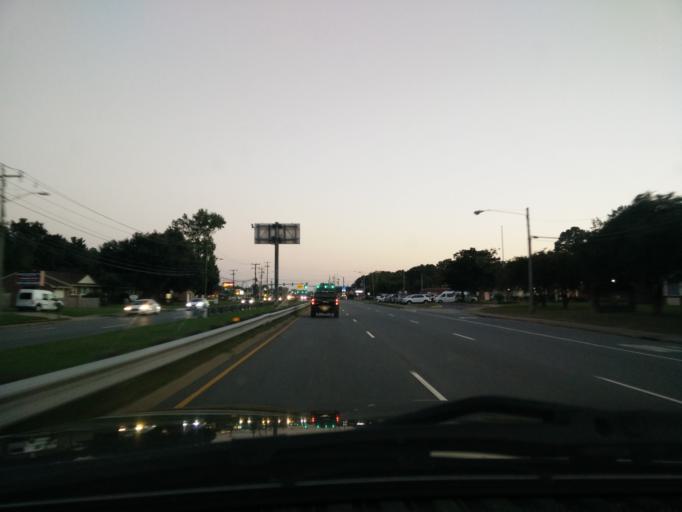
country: US
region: Virginia
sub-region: City of Chesapeake
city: Chesapeake
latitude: 36.7597
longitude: -76.2501
